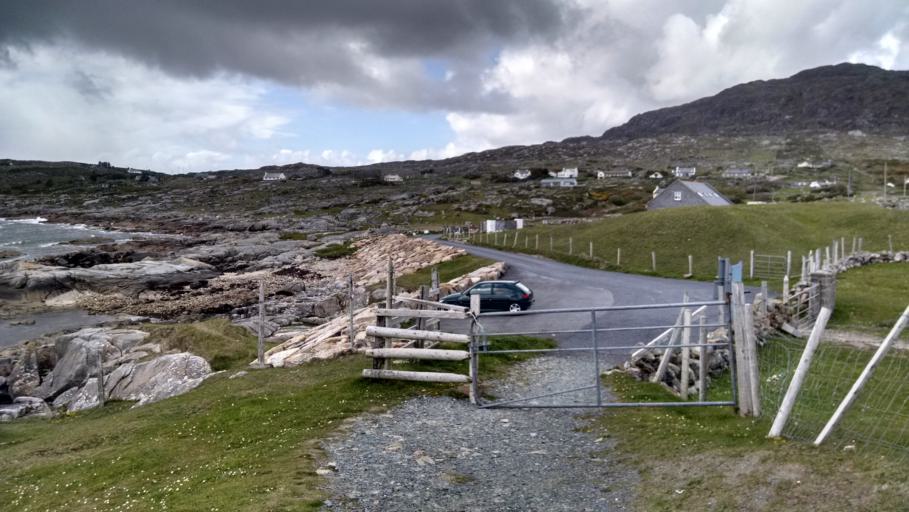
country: IE
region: Connaught
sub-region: County Galway
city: Clifden
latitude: 53.3807
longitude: -9.9632
